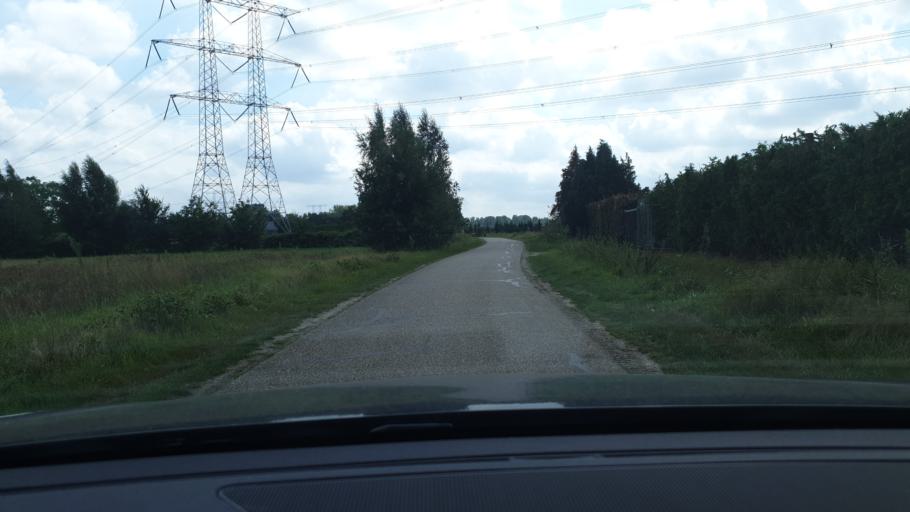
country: NL
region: North Brabant
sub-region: Gemeente Son en Breugel
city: Son
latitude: 51.4996
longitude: 5.4999
